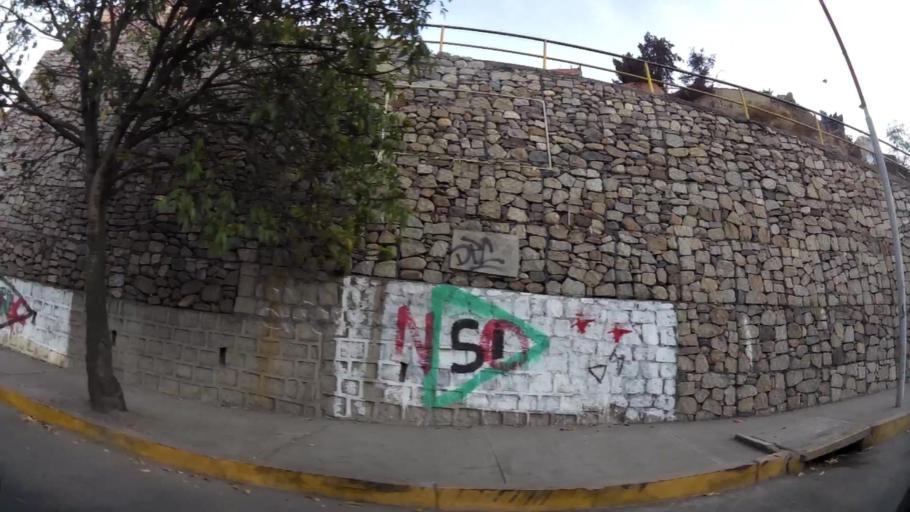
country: BO
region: La Paz
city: La Paz
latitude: -16.5143
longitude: -68.1253
